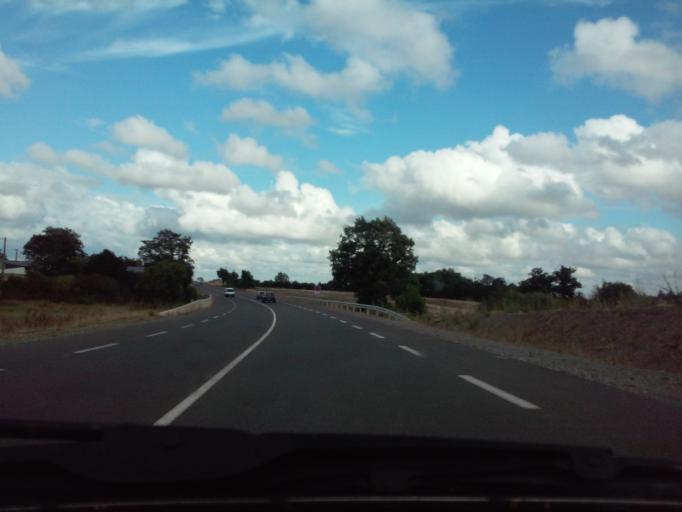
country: FR
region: Pays de la Loire
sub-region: Departement de la Mayenne
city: Argentre
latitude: 48.0643
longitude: -0.6210
